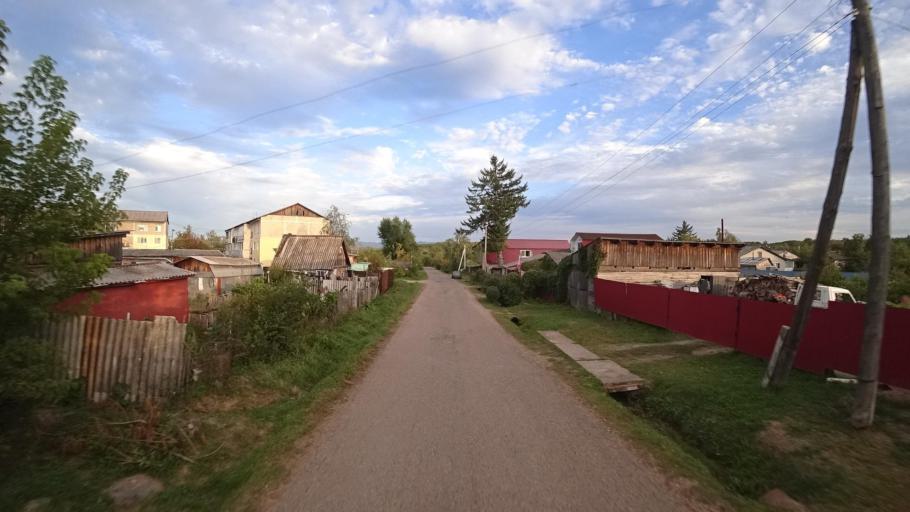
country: RU
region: Primorskiy
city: Yakovlevka
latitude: 44.4222
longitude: 133.4722
